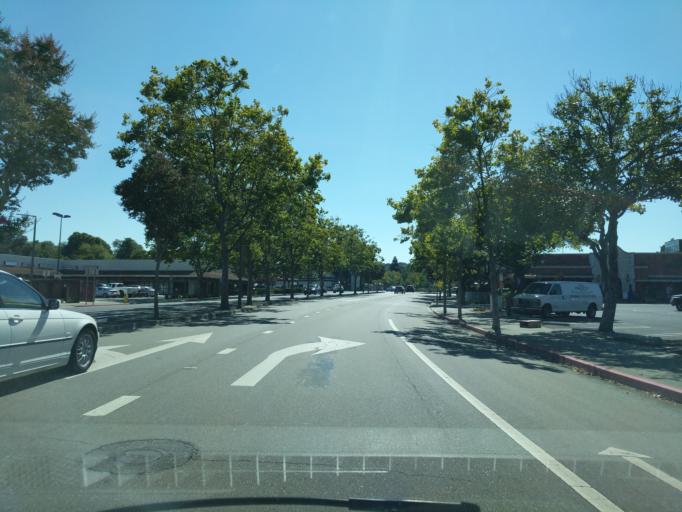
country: US
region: California
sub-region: Alameda County
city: Dublin
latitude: 37.7061
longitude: -121.9352
